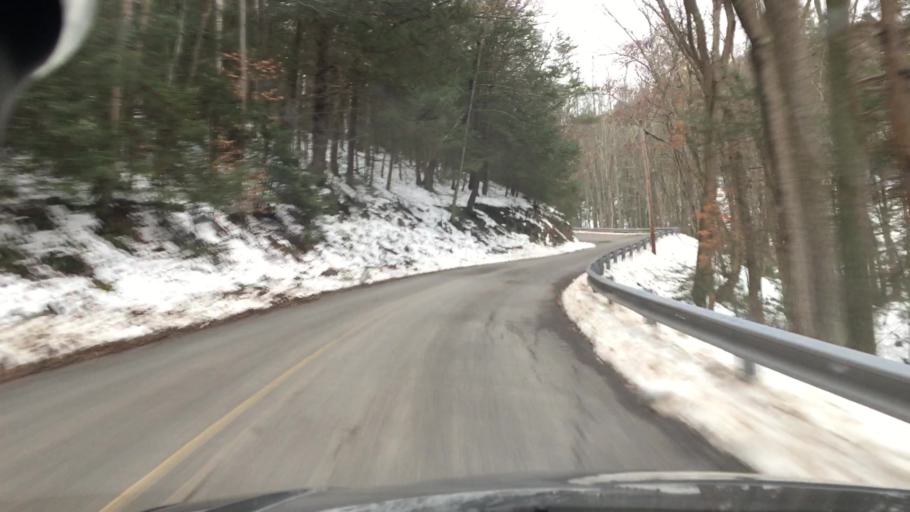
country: US
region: Pennsylvania
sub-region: Luzerne County
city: Conyngham
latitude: 41.0066
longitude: -76.1313
